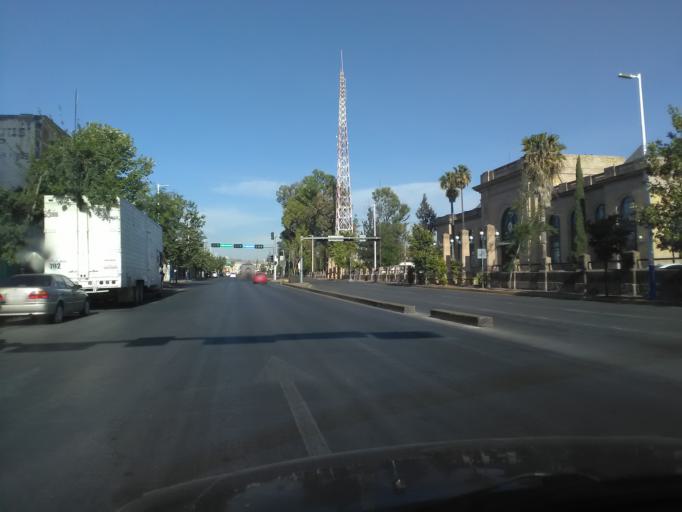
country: MX
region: Durango
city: Victoria de Durango
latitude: 24.0347
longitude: -104.6717
